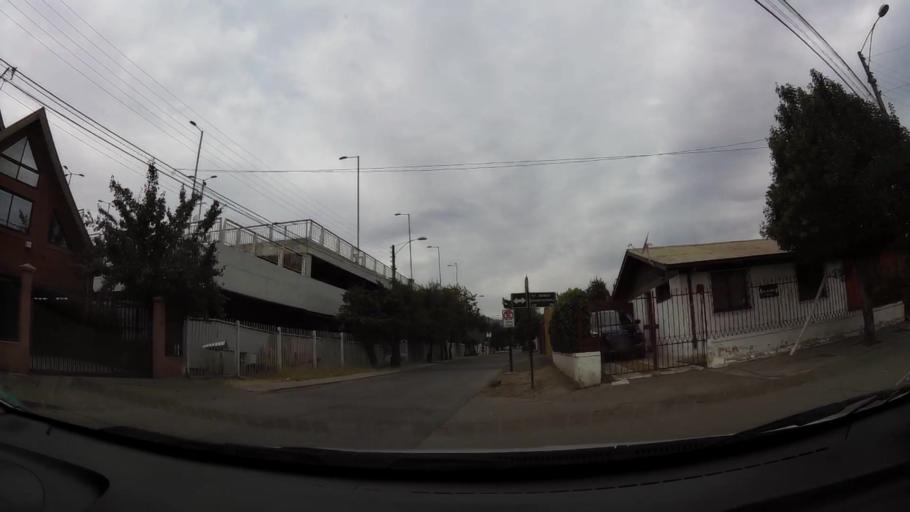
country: CL
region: O'Higgins
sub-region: Provincia de Cachapoal
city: Rancagua
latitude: -34.1557
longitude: -70.7393
